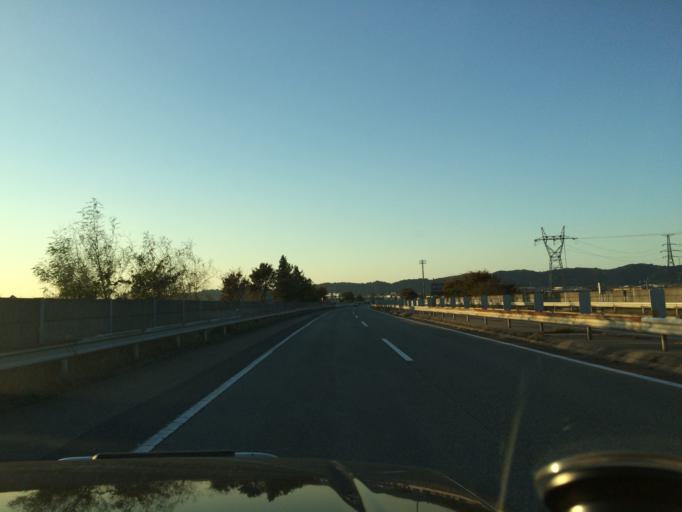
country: JP
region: Toyama
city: Toyama-shi
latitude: 36.6655
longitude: 137.1864
